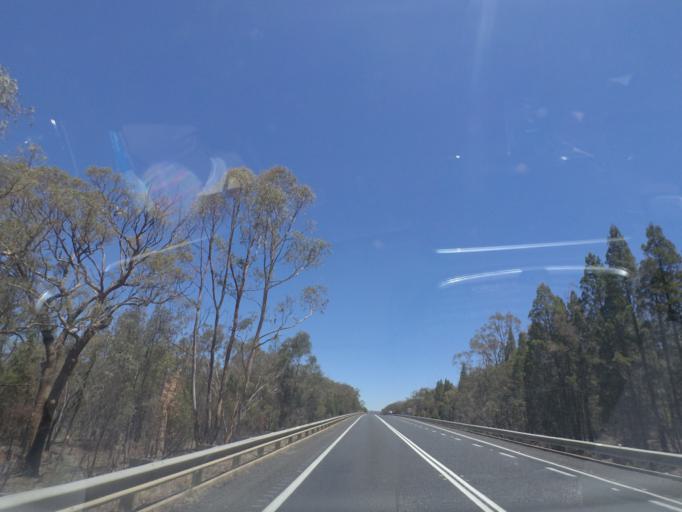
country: AU
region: New South Wales
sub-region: Warrumbungle Shire
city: Coonabarabran
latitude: -31.2306
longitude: 149.3196
